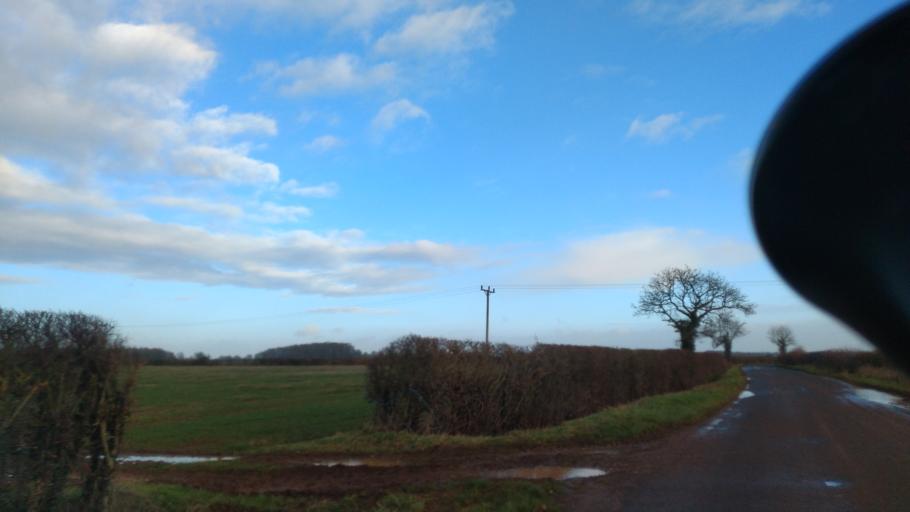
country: GB
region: England
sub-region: Wiltshire
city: Corsham
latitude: 51.4537
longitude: -2.1687
